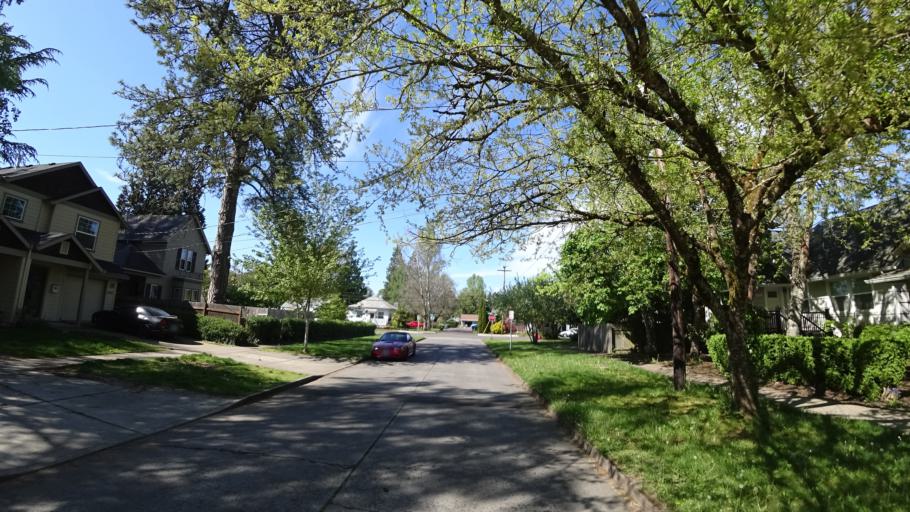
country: US
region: Oregon
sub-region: Washington County
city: Hillsboro
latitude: 45.5279
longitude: -122.9878
